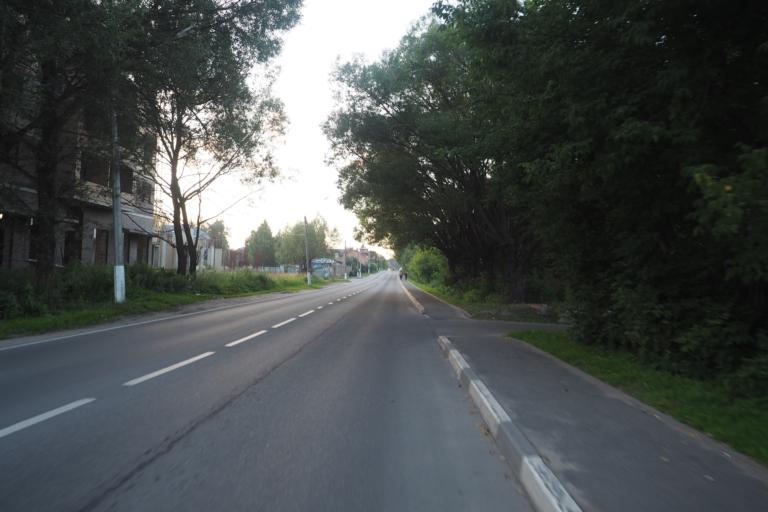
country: RU
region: Moskovskaya
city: Staraya Kupavna
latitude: 55.8126
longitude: 38.1745
